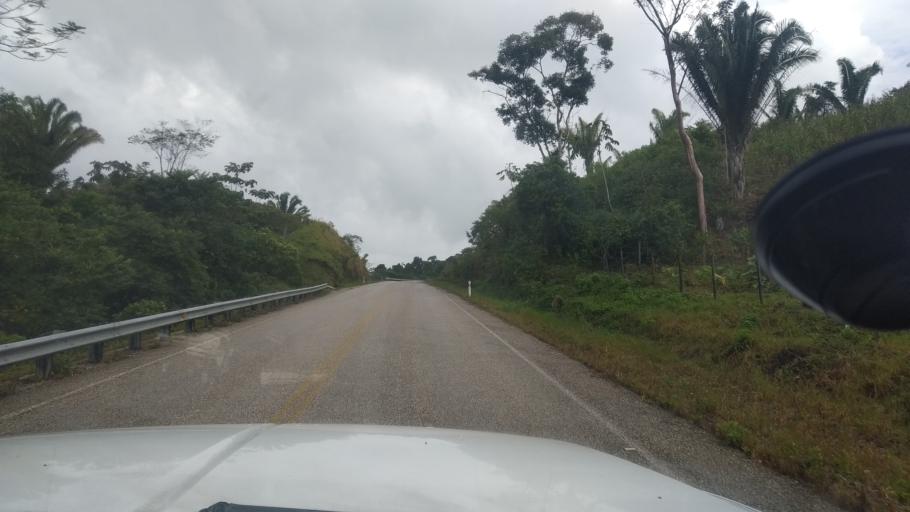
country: GT
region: Peten
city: San Luis
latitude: 16.1951
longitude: -89.1681
